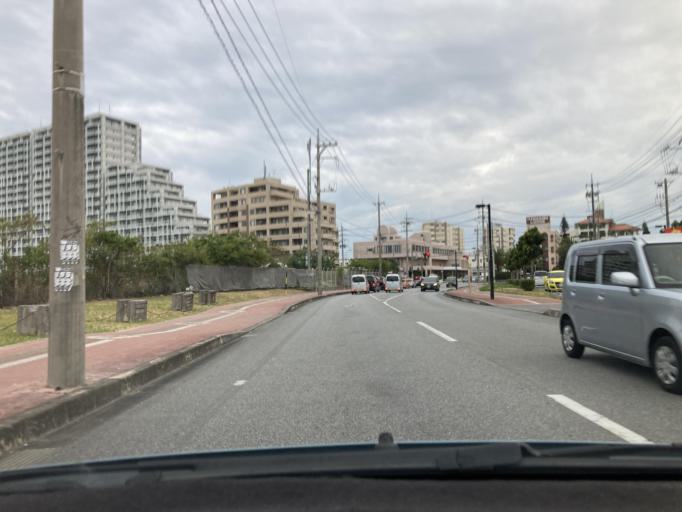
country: JP
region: Okinawa
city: Chatan
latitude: 26.3240
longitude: 127.7548
